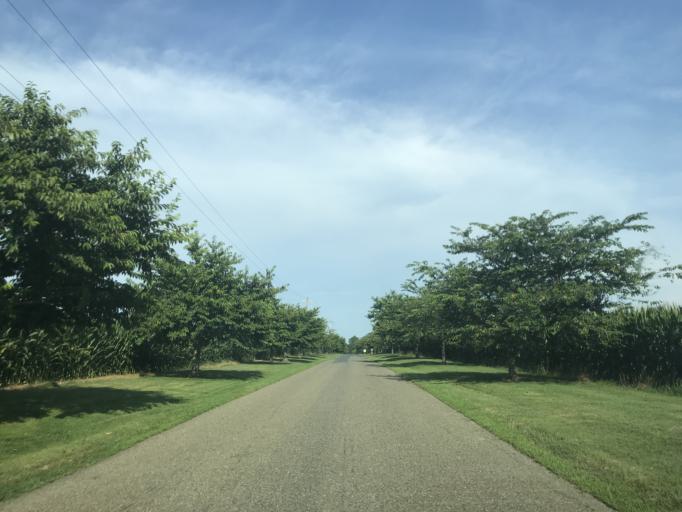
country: US
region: Maryland
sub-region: Harford County
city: Havre de Grace
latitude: 39.5225
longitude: -76.1215
